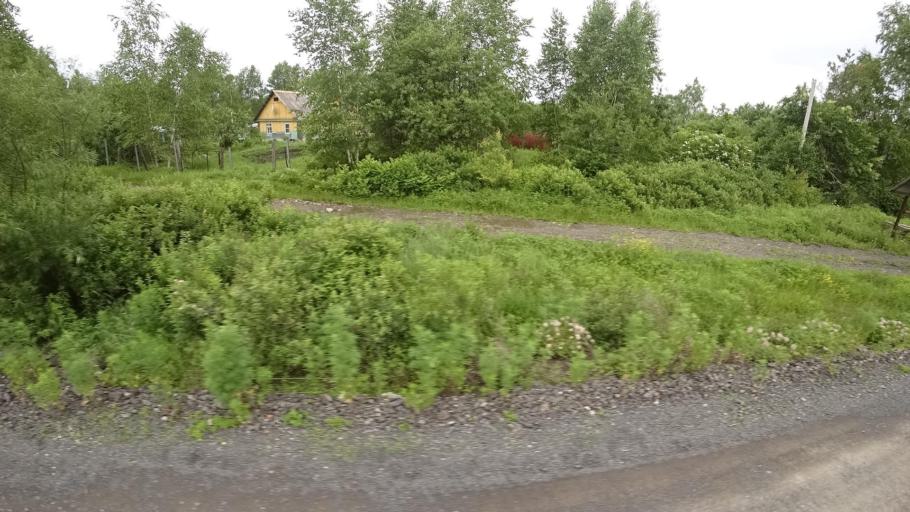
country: RU
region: Khabarovsk Krai
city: Amursk
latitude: 49.9024
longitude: 136.1374
